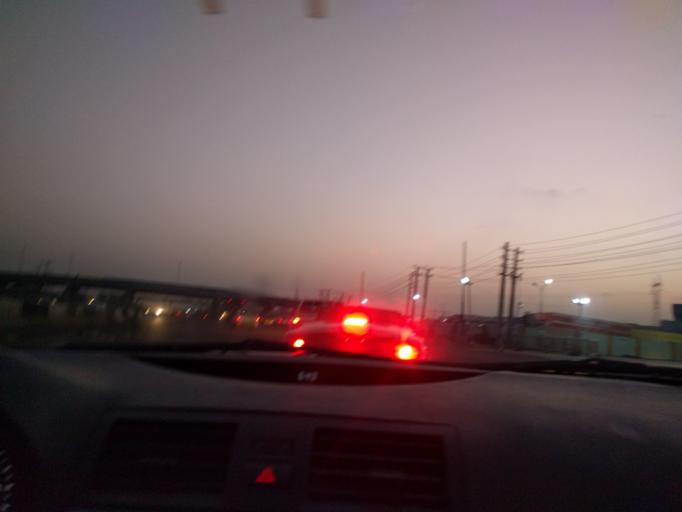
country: NG
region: Lagos
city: Surulere
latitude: 6.5088
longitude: 3.3247
